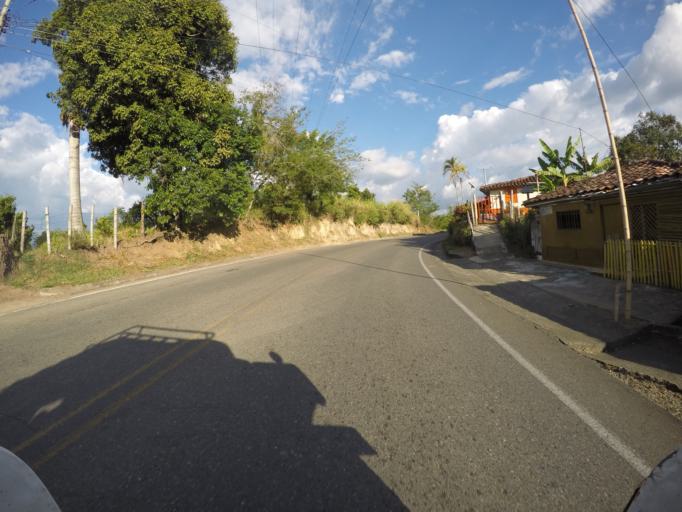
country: CO
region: Valle del Cauca
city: Alcala
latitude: 4.6917
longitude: -75.8220
